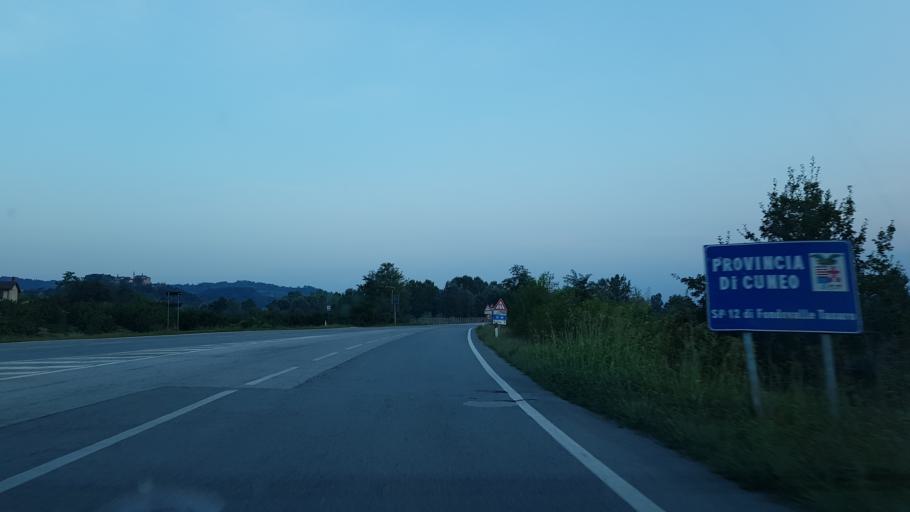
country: IT
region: Piedmont
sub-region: Provincia di Cuneo
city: Monchiero Borgonuovo
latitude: 44.5802
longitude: 7.9090
